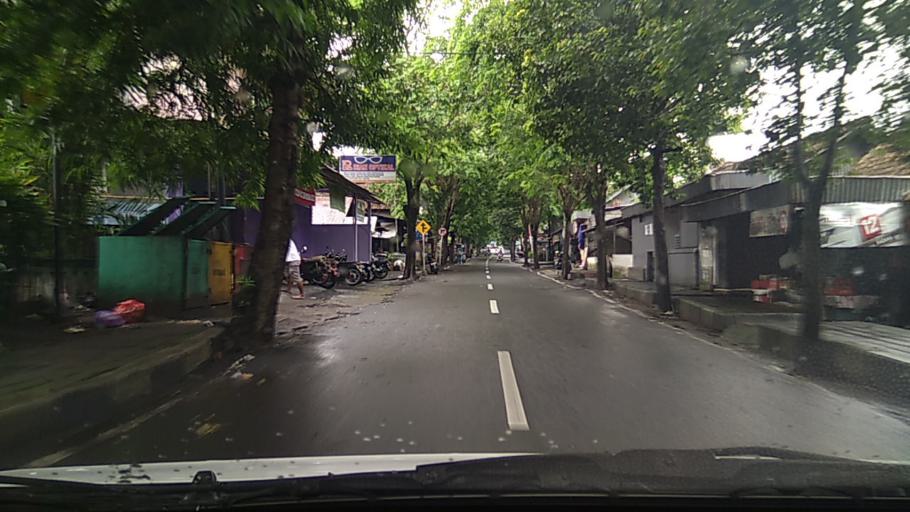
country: ID
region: Bali
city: Karangasem
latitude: -8.4475
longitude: 115.6123
